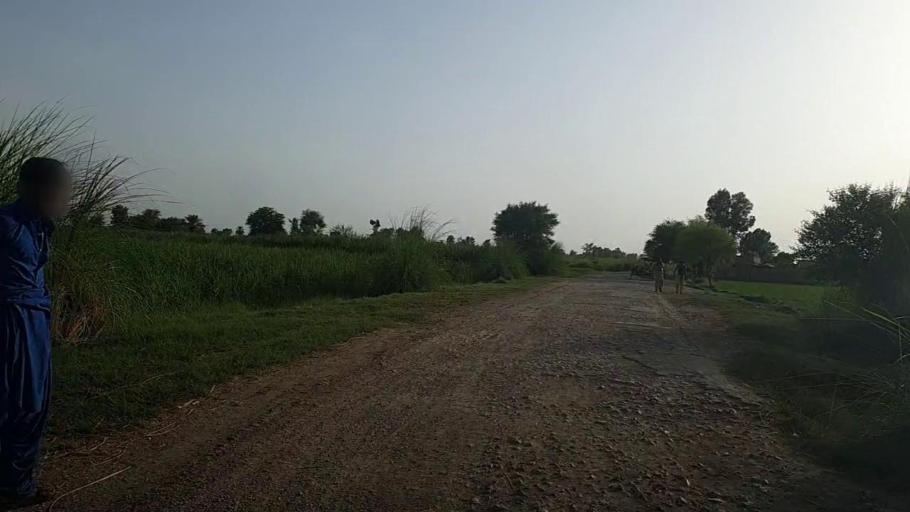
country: PK
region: Sindh
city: Naushahro Firoz
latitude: 26.8084
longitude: 68.1305
